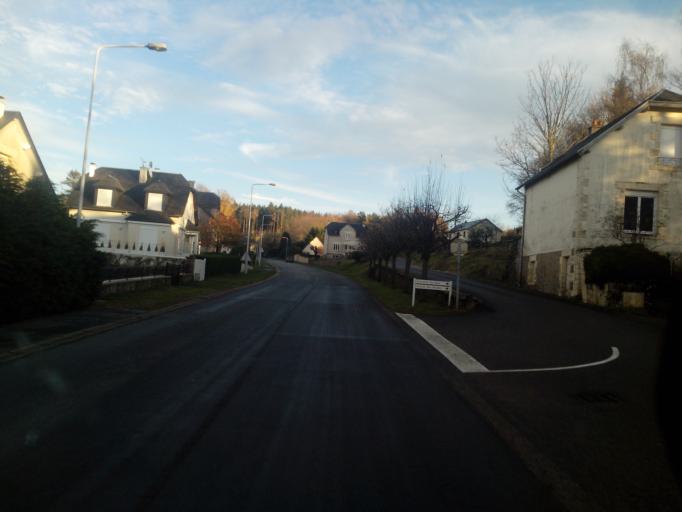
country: FR
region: Limousin
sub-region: Departement de la Correze
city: Bugeat
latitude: 45.5964
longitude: 1.9342
